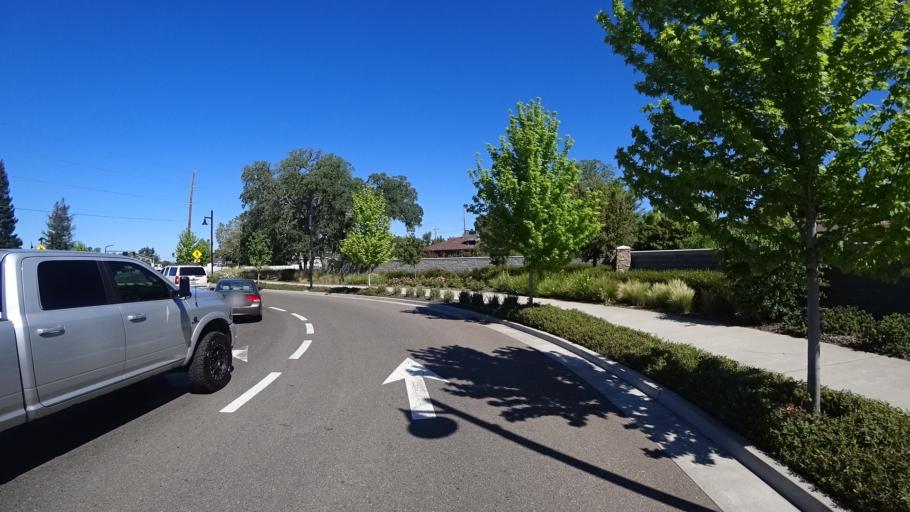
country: US
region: California
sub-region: Placer County
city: Rocklin
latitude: 38.7889
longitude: -121.2315
